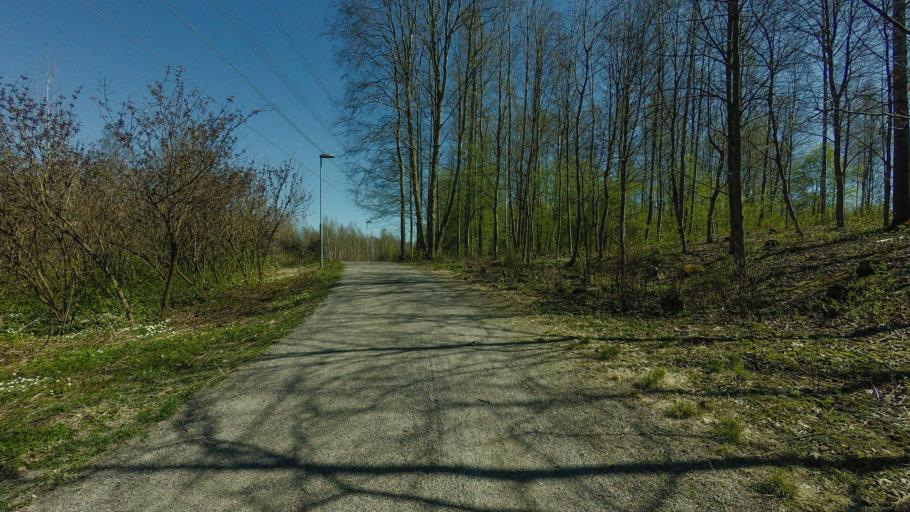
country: FI
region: Uusimaa
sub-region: Helsinki
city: Vantaa
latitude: 60.2311
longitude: 25.1166
